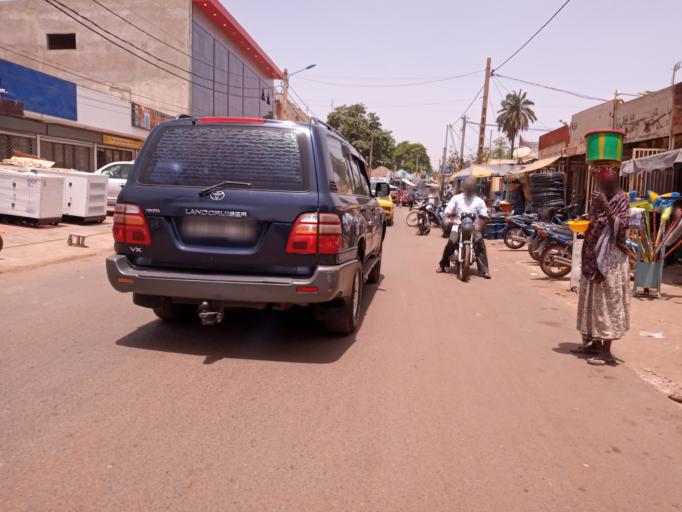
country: ML
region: Bamako
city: Bamako
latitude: 12.6369
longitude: -8.0017
